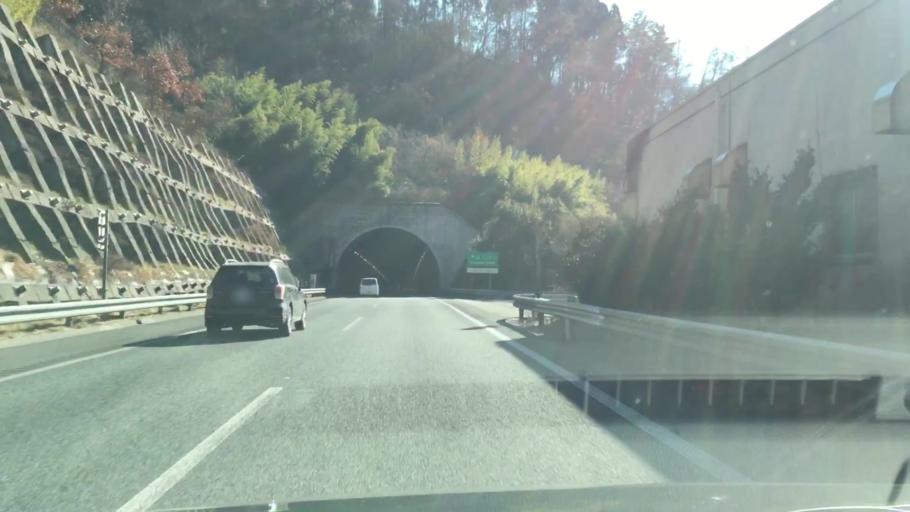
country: JP
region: Nagano
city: Ueda
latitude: 36.4777
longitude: 138.1923
